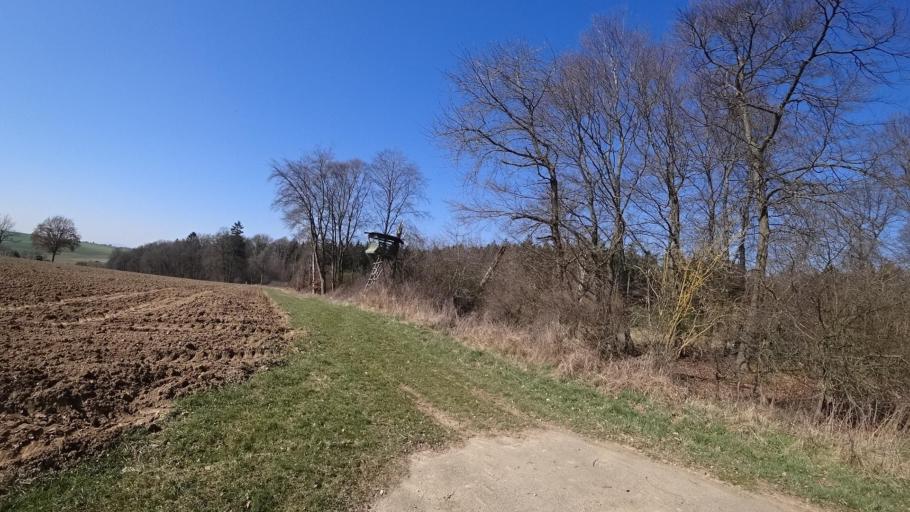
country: DE
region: Rheinland-Pfalz
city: Wahlbach
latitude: 50.0061
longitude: 7.5911
